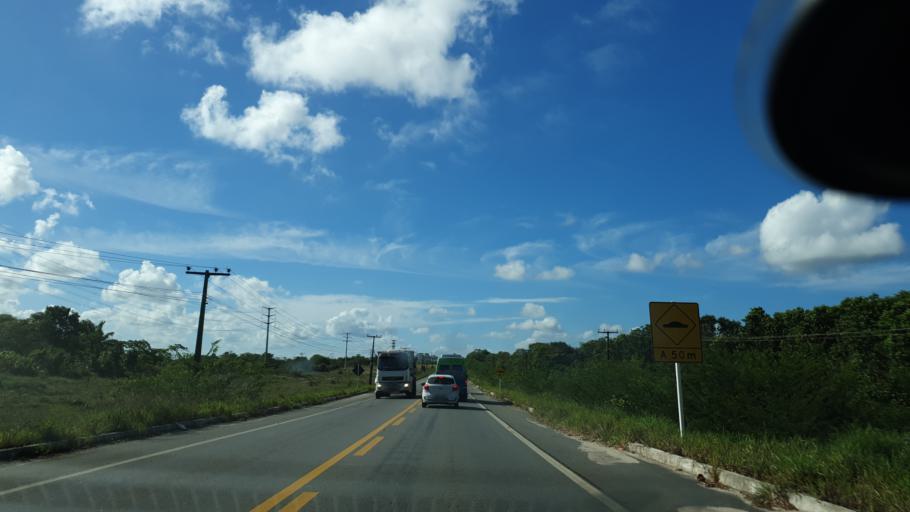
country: BR
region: Bahia
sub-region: Camacari
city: Camacari
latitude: -12.6882
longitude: -38.2283
